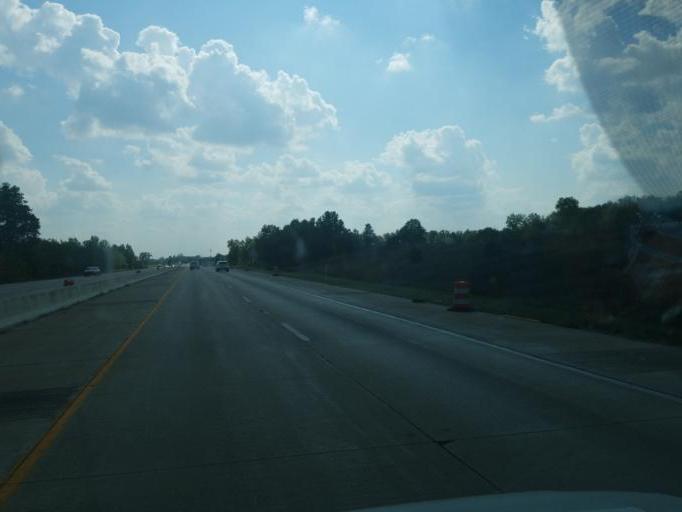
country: US
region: Indiana
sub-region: Allen County
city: Leo-Cedarville
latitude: 41.1472
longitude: -85.0149
